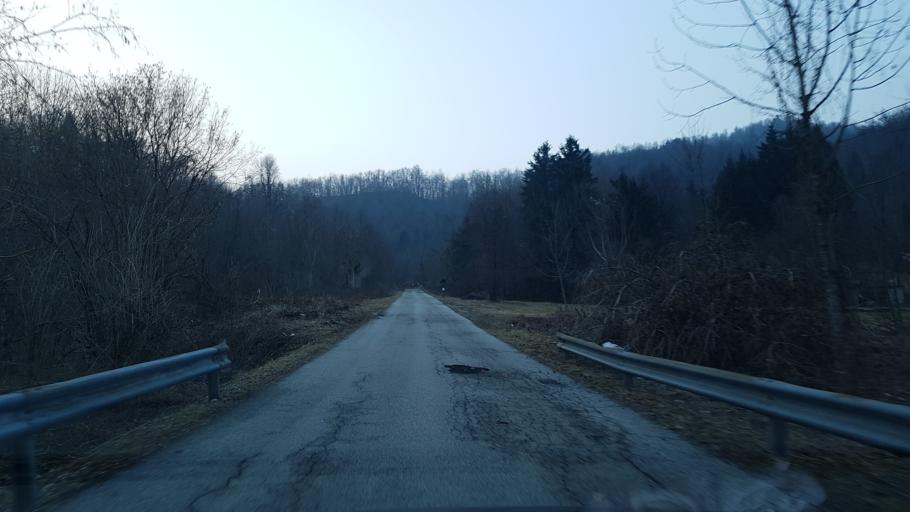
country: IT
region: Friuli Venezia Giulia
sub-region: Provincia di Udine
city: Taipana
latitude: 46.2157
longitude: 13.3977
